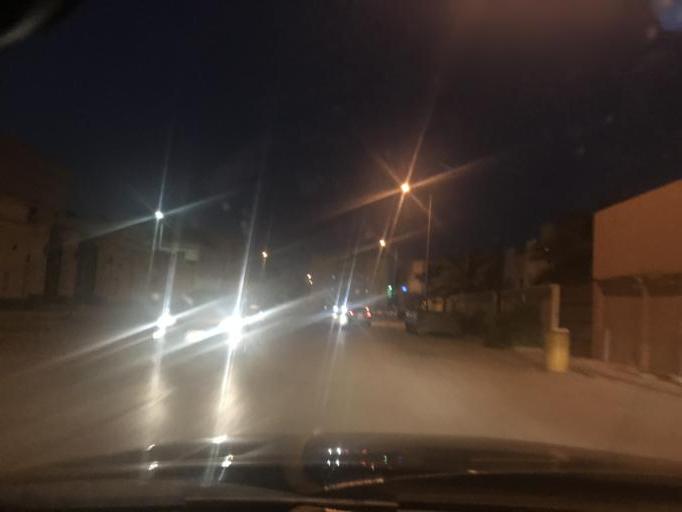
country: SA
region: Ar Riyad
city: Riyadh
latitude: 24.7499
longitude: 46.7844
